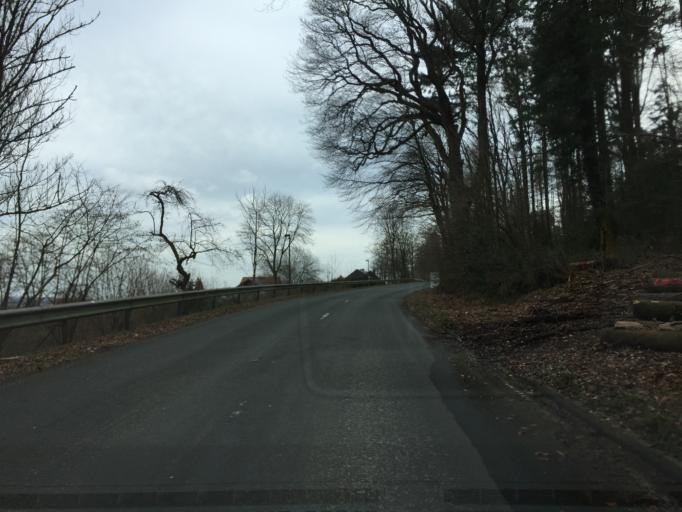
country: DE
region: North Rhine-Westphalia
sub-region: Regierungsbezirk Detmold
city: Detmold
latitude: 51.9194
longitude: 8.8351
